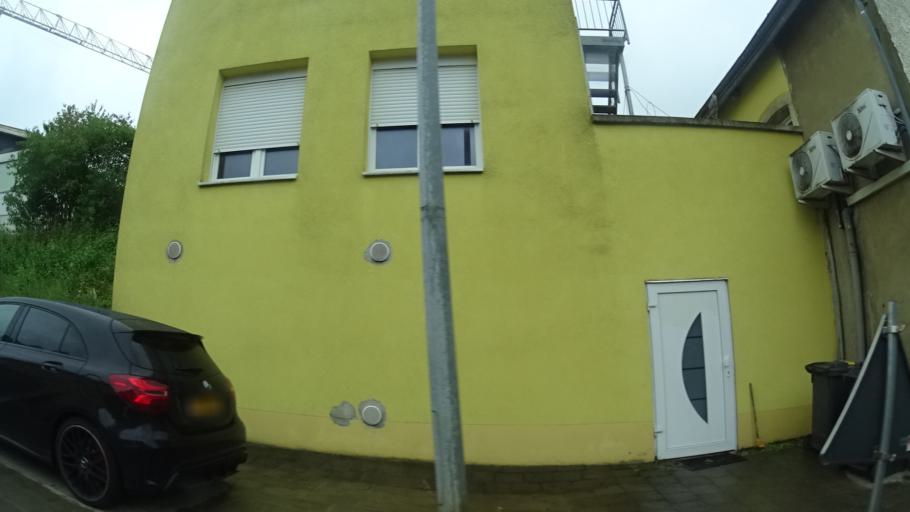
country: LU
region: Luxembourg
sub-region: Canton d'Esch-sur-Alzette
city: Sanem
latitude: 49.5489
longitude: 5.9296
